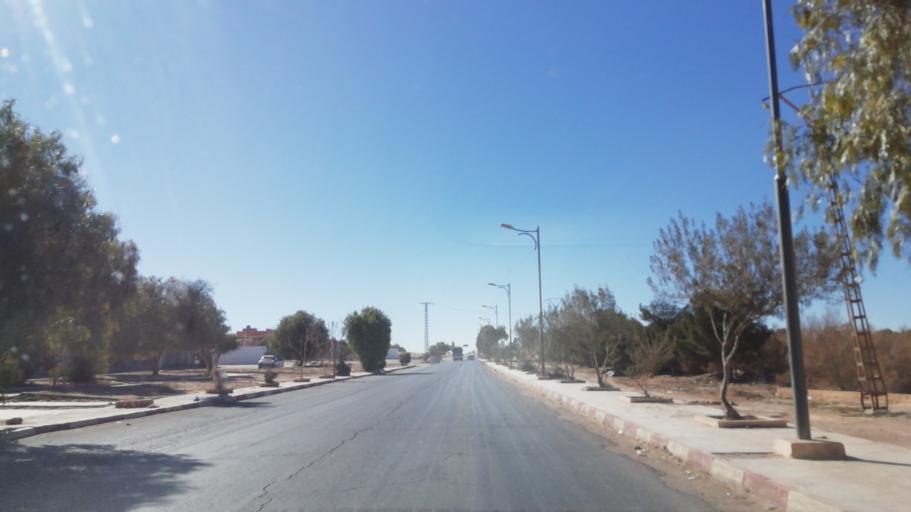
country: DZ
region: Saida
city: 'Ain el Hadjar
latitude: 34.0398
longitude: 0.0808
